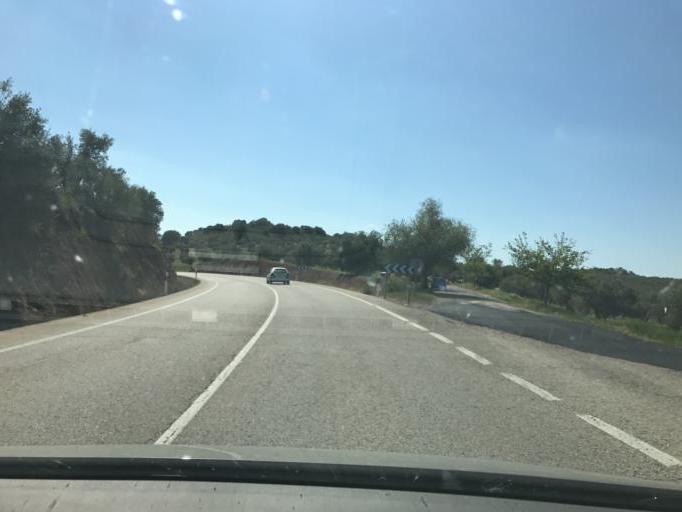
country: ES
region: Andalusia
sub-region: Province of Cordoba
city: Fuente-Tojar
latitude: 37.5729
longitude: -4.1750
